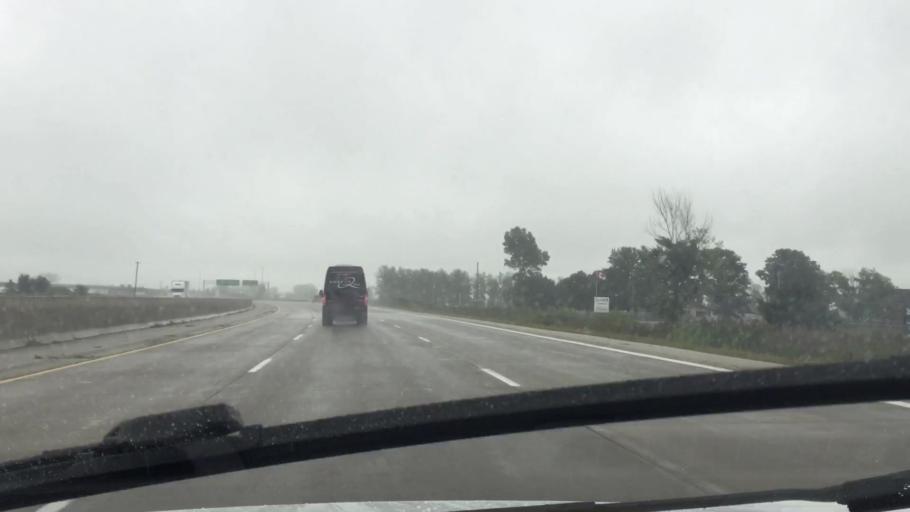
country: CA
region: Ontario
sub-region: Lambton County
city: Walpole Island
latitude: 42.2595
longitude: -82.4643
